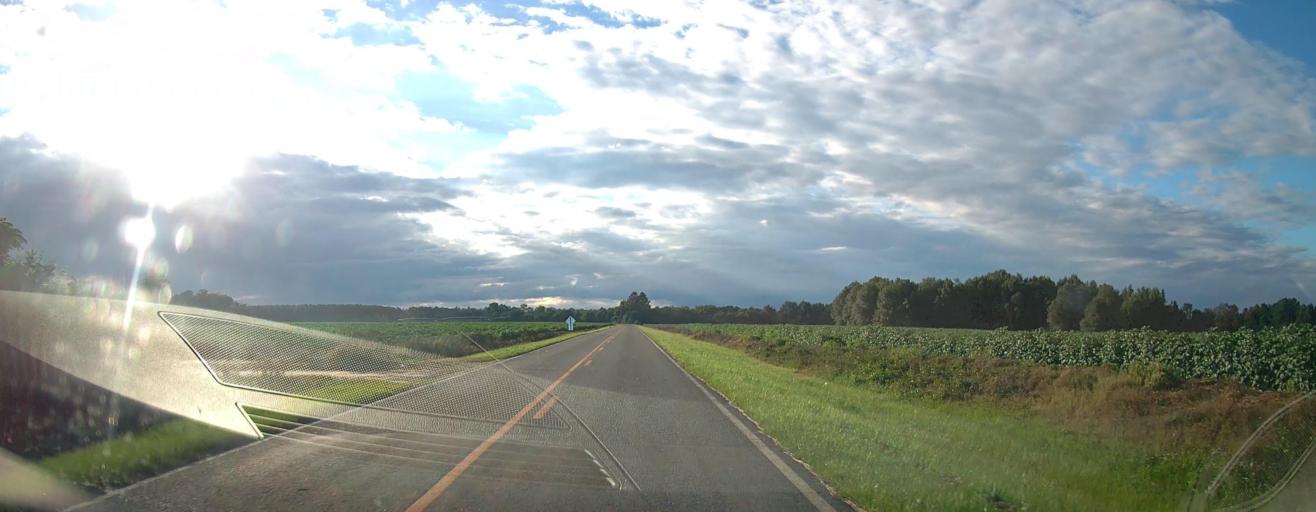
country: US
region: Georgia
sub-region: Pulaski County
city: Hawkinsville
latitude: 32.2838
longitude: -83.5404
